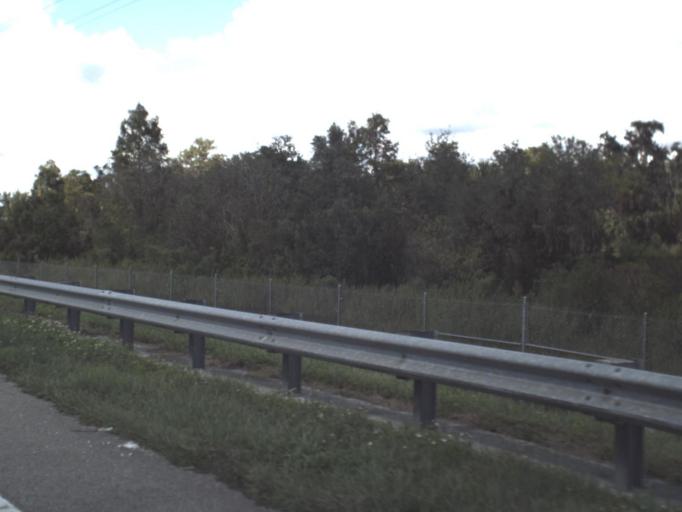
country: US
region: Florida
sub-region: DeSoto County
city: Arcadia
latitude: 27.2563
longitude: -81.9703
